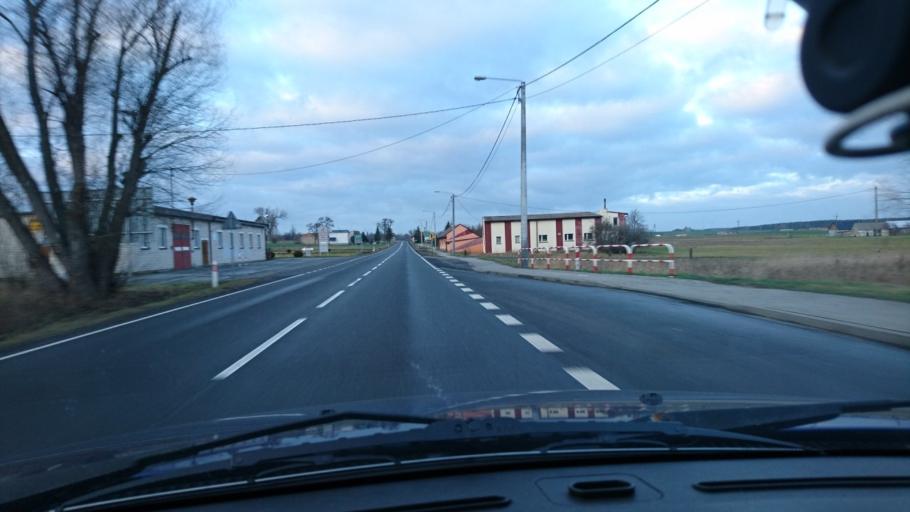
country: PL
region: Greater Poland Voivodeship
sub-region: Powiat ostrzeszowski
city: Ostrzeszow
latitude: 51.3558
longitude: 17.9471
